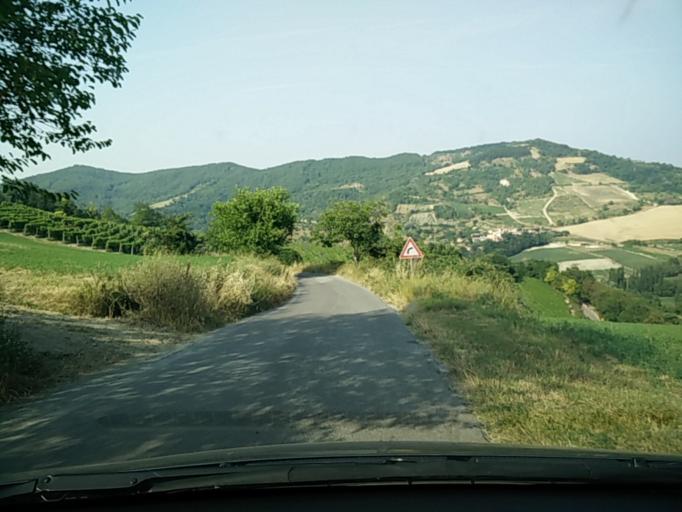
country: IT
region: Lombardy
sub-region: Provincia di Pavia
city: Susella
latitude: 44.9313
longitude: 9.1130
